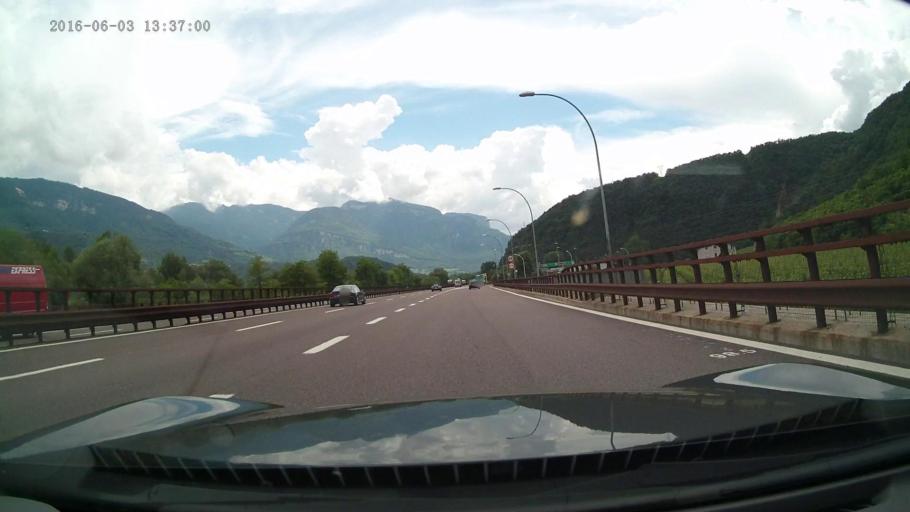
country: IT
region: Trentino-Alto Adige
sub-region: Bolzano
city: Ora
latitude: 46.3629
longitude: 11.2896
